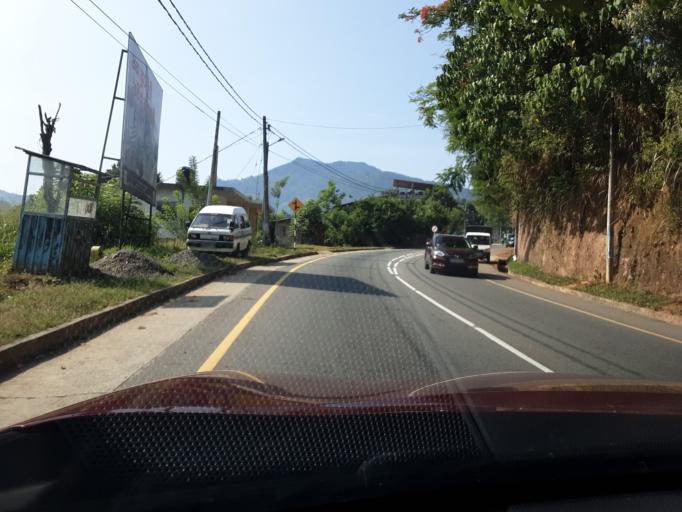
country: LK
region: Uva
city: Badulla
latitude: 6.9850
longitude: 81.0787
